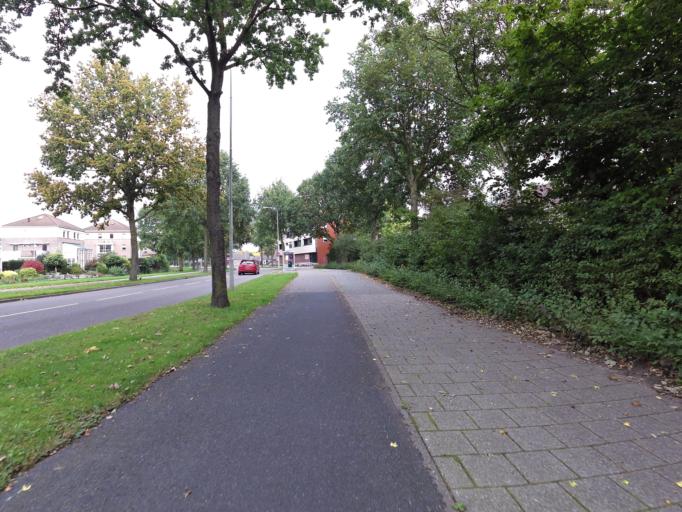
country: NL
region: Gelderland
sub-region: Gemeente Westervoort
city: Westervoort
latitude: 51.9469
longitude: 5.9774
